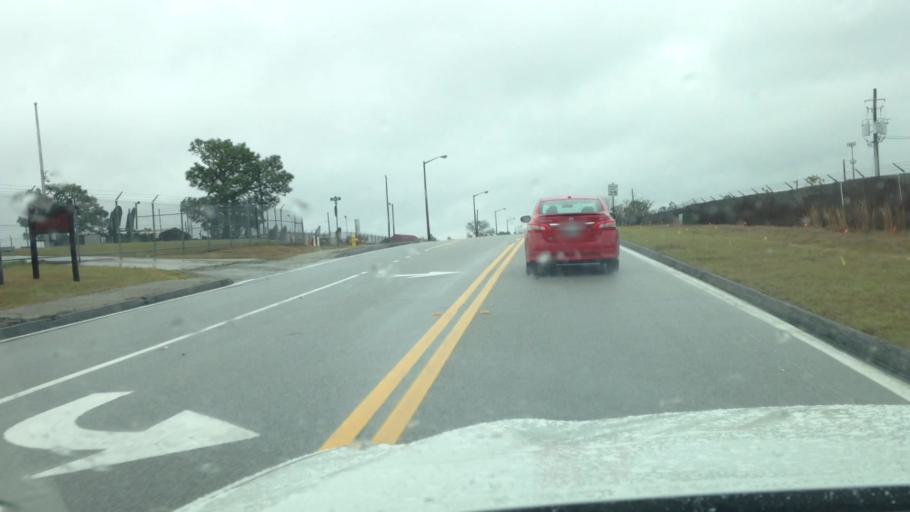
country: US
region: Georgia
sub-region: Columbia County
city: Grovetown
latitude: 33.4162
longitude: -82.1605
